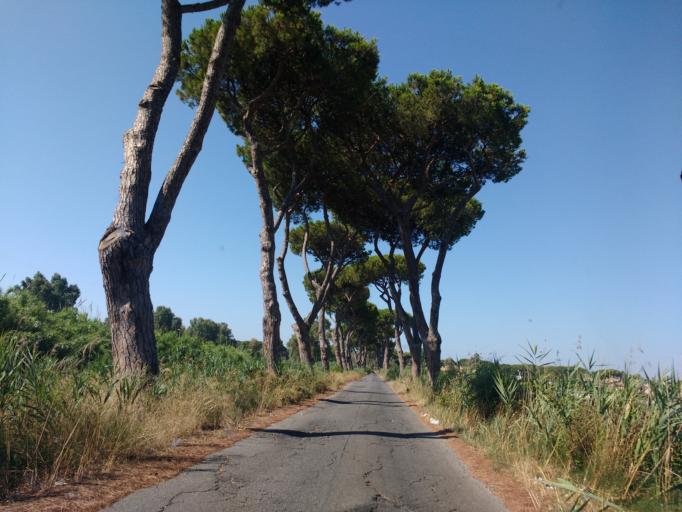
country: IT
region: Latium
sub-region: Citta metropolitana di Roma Capitale
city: Acilia-Castel Fusano-Ostia Antica
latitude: 41.7480
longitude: 12.3250
